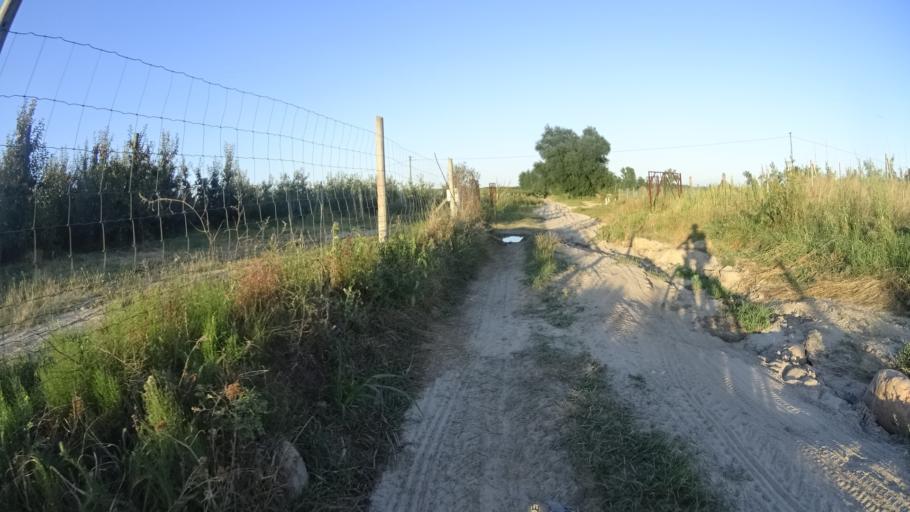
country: PL
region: Masovian Voivodeship
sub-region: Powiat bialobrzeski
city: Wysmierzyce
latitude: 51.6611
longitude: 20.8244
